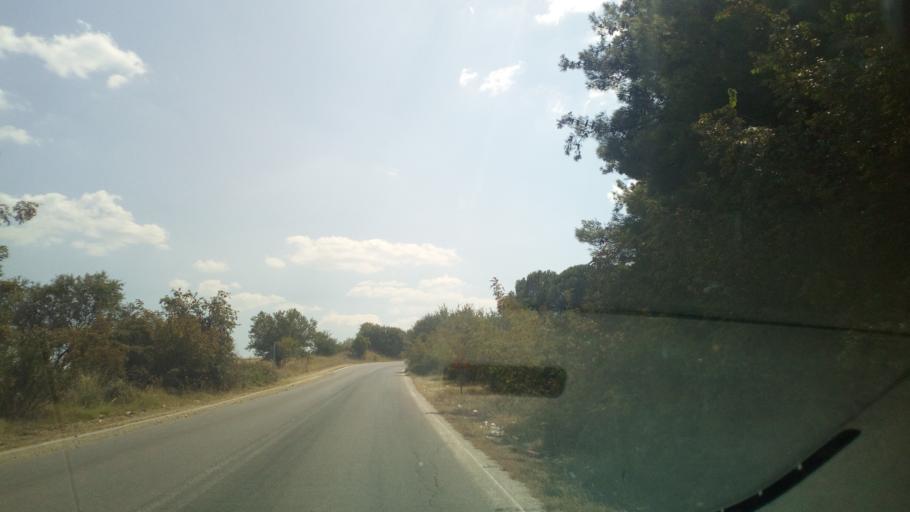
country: GR
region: Central Macedonia
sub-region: Nomos Thessalonikis
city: Agios Vasileios
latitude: 40.6552
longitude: 23.1141
